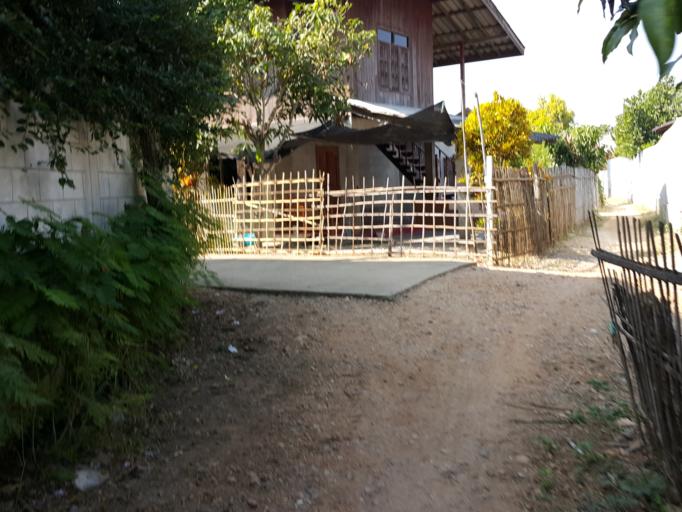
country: TH
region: Lamphun
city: Wiang Nong Long
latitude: 18.3793
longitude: 98.7500
